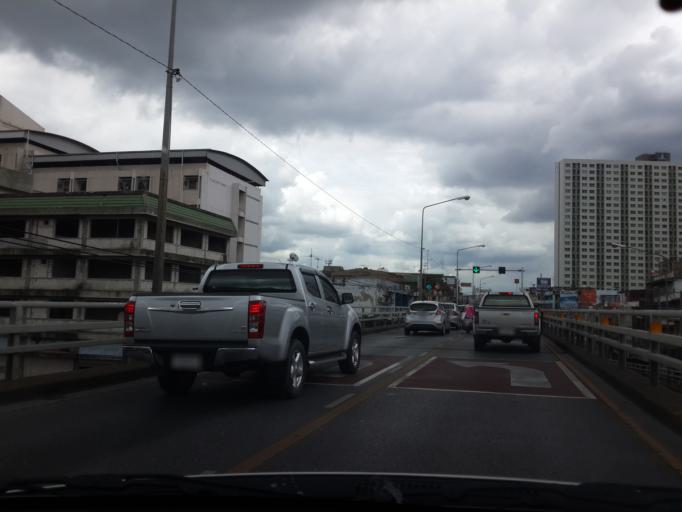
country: TH
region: Bangkok
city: Bang Kapi
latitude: 13.7629
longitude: 100.6469
